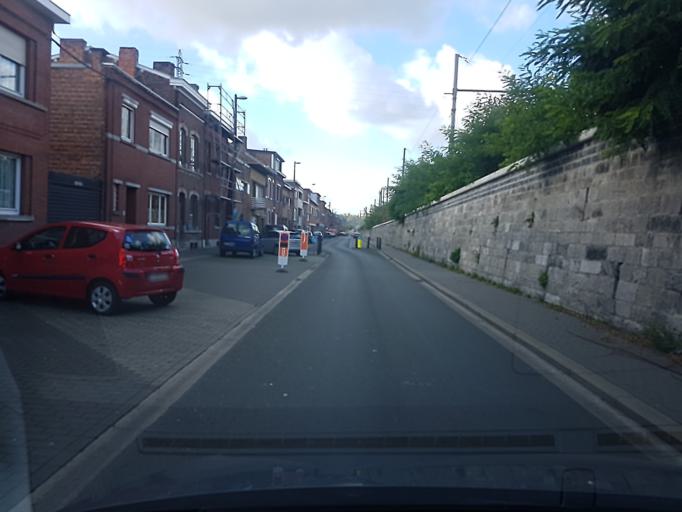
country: BE
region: Wallonia
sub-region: Province de Liege
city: Liege
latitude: 50.6131
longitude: 5.5978
